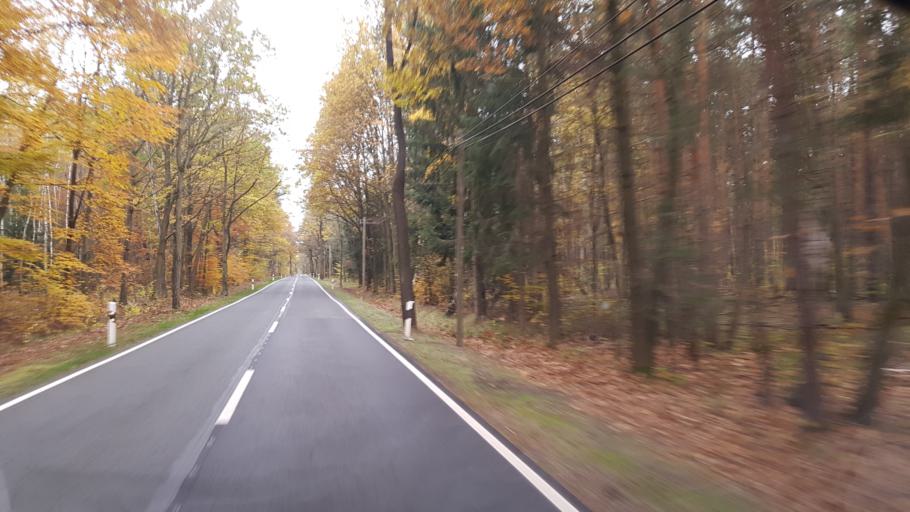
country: DE
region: Brandenburg
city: Crinitz
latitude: 51.7488
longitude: 13.7920
